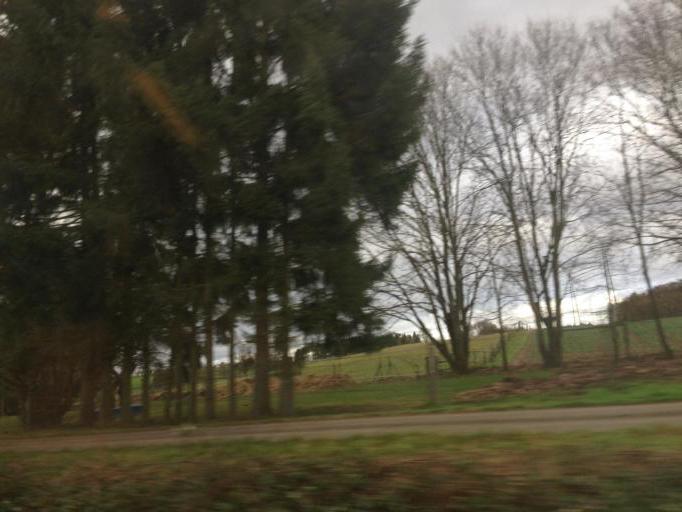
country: DE
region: Hesse
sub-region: Regierungsbezirk Giessen
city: Lich
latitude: 50.5257
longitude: 8.7590
